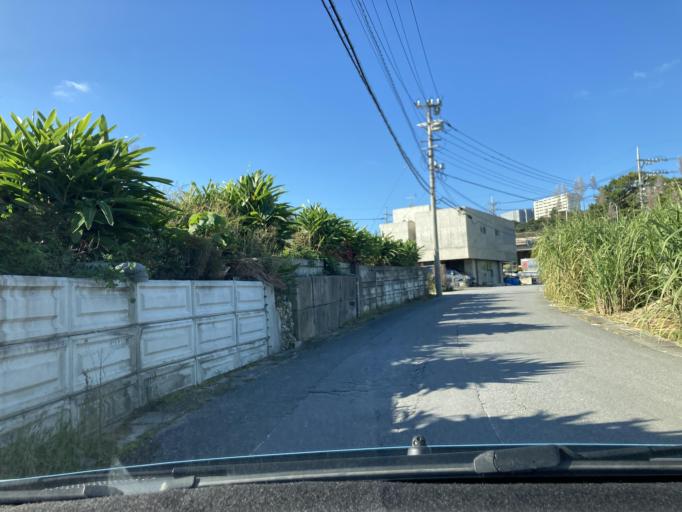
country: JP
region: Okinawa
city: Ginowan
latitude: 26.2307
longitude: 127.7404
